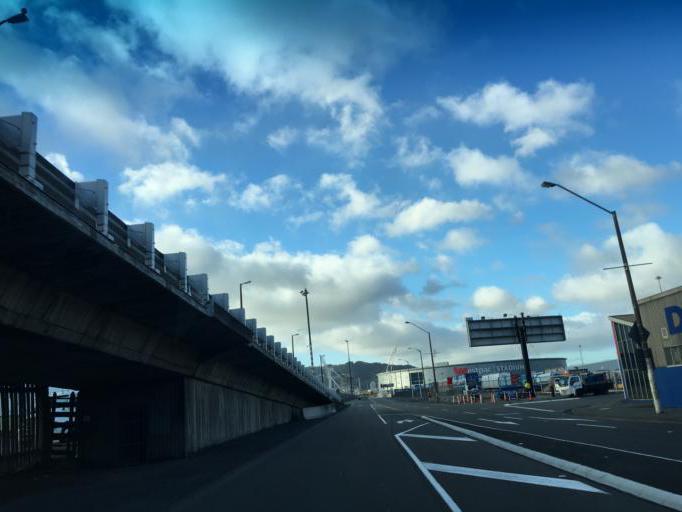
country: NZ
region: Wellington
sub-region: Wellington City
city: Wellington
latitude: -41.2668
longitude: 174.7855
